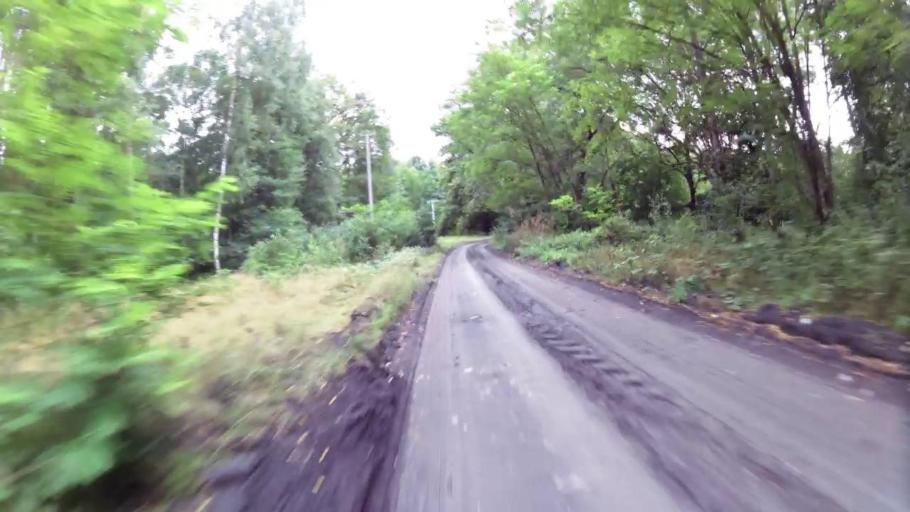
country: PL
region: West Pomeranian Voivodeship
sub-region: Powiat mysliborski
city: Debno
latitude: 52.8003
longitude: 14.7180
